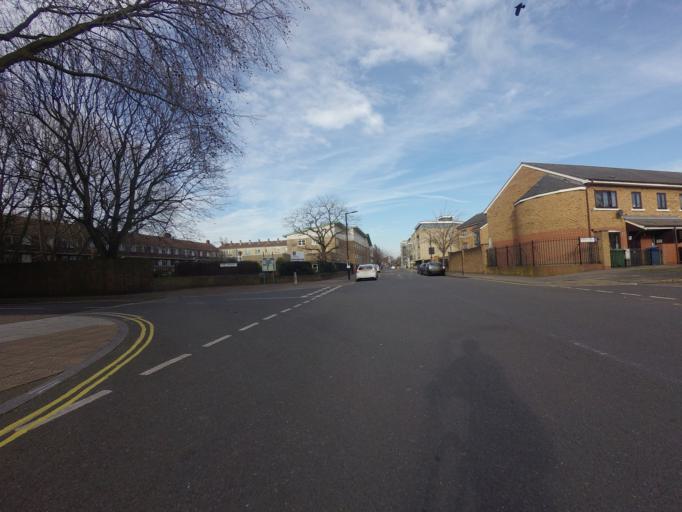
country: GB
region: England
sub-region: Greater London
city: Camberwell
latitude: 51.4805
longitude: -0.0741
